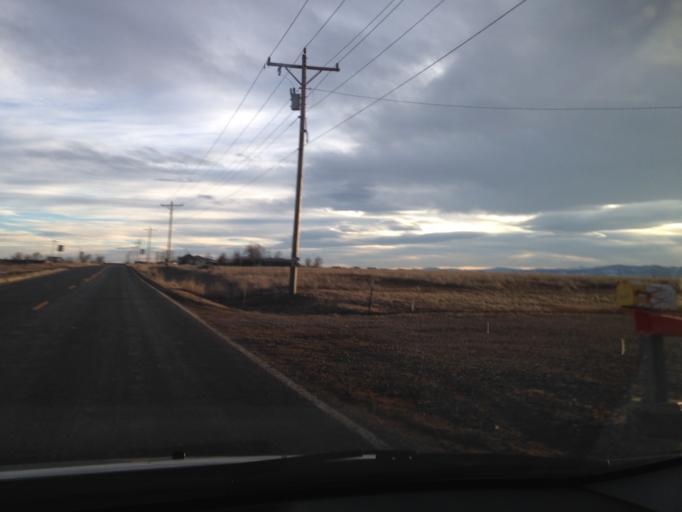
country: US
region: Colorado
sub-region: Weld County
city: Frederick
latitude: 40.1021
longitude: -104.9989
